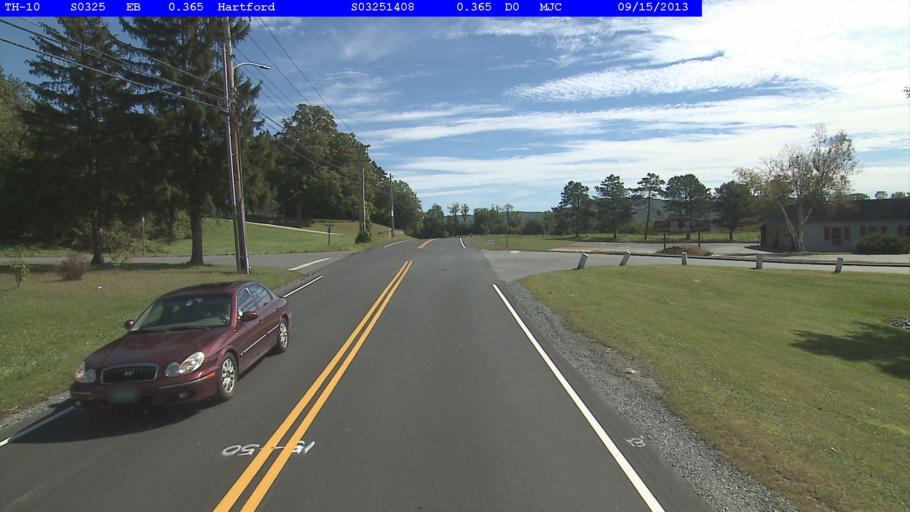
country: US
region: Vermont
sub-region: Windsor County
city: White River Junction
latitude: 43.6442
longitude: -72.3292
